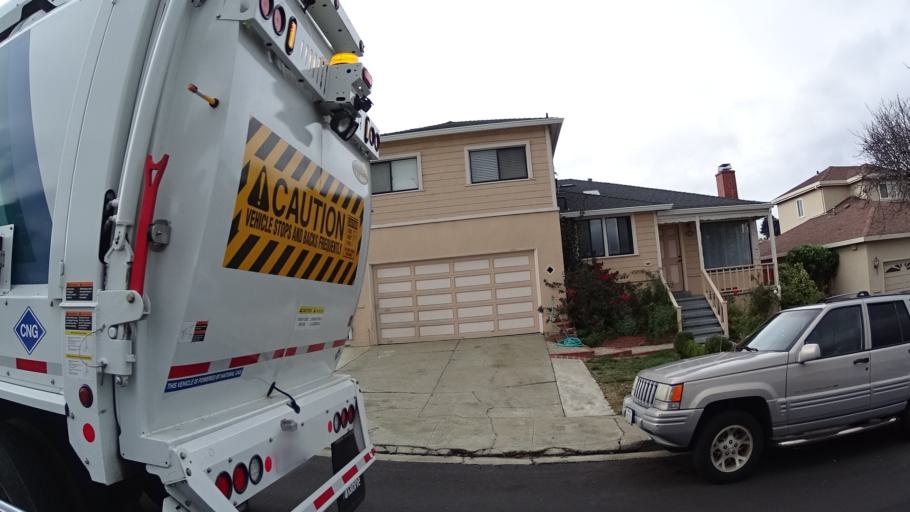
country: US
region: California
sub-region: San Mateo County
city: San Bruno
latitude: 37.6385
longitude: -122.4309
